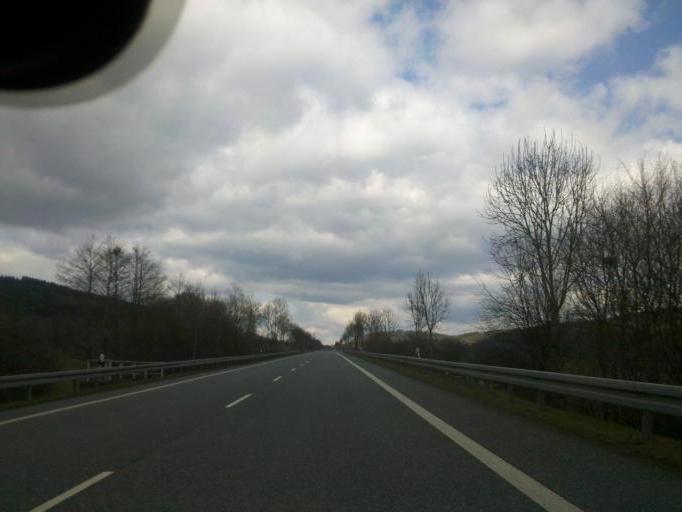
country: DE
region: Hesse
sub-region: Regierungsbezirk Giessen
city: Siegbach
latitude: 50.8107
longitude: 8.3569
